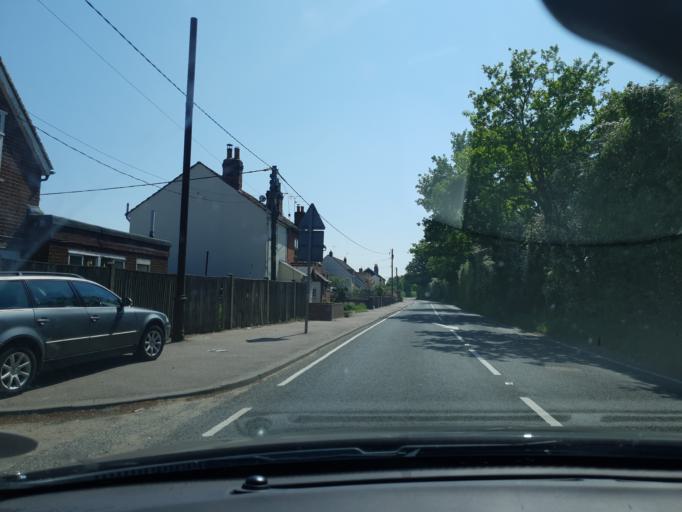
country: GB
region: England
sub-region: Essex
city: Great Bentley
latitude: 51.8488
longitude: 1.0357
